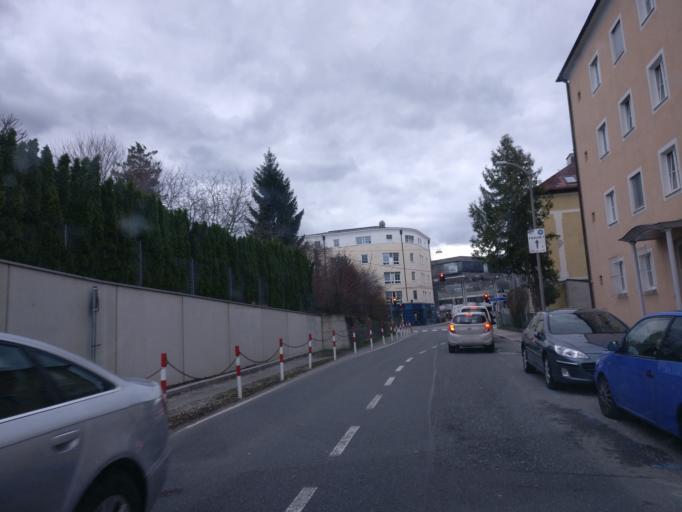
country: AT
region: Salzburg
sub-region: Politischer Bezirk Salzburg-Umgebung
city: Bergheim
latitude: 47.8232
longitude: 13.0437
